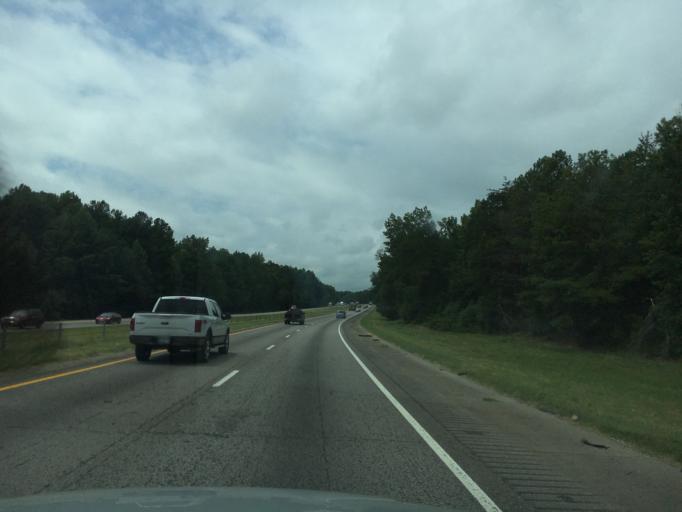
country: US
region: Georgia
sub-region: Banks County
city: Maysville
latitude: 34.2123
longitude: -83.5333
